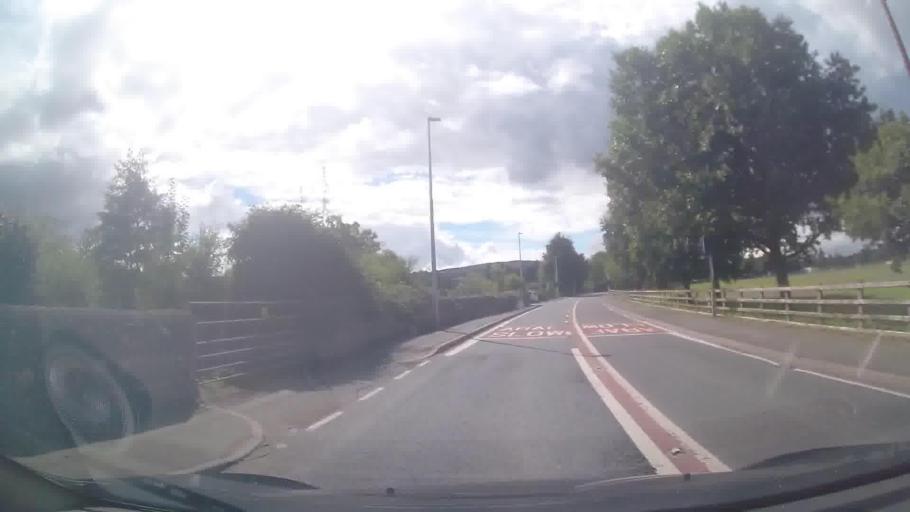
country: GB
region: Wales
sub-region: Sir Powys
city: Builth Wells
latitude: 52.1552
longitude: -3.3967
